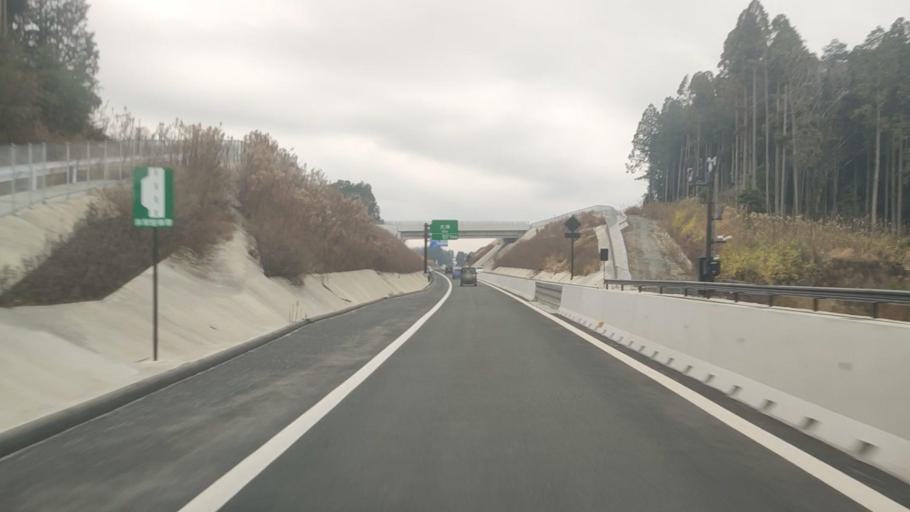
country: JP
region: Kumamoto
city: Ozu
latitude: 32.8984
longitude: 130.9019
